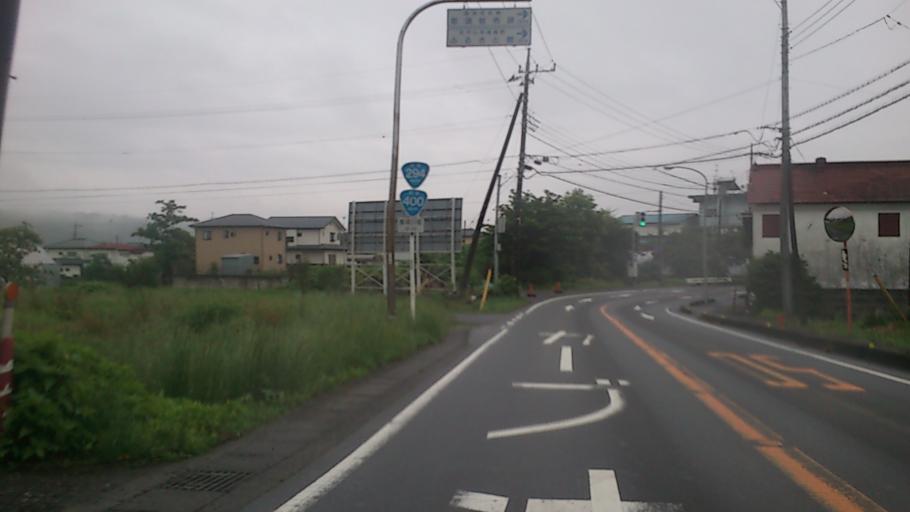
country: JP
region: Tochigi
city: Karasuyama
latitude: 36.7756
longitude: 140.1246
